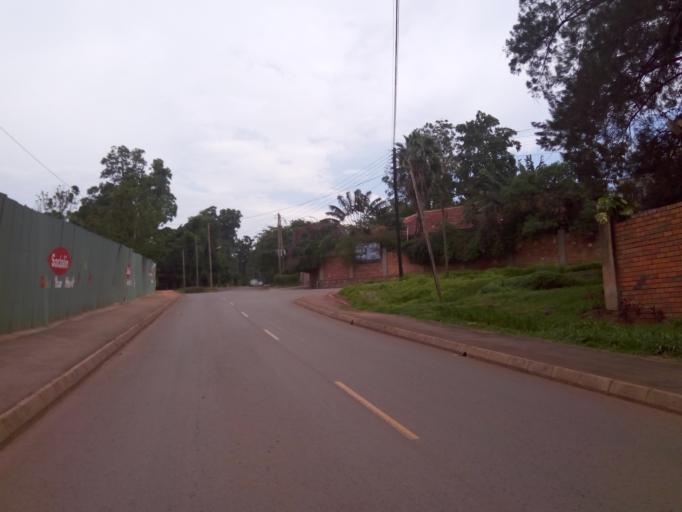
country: UG
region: Central Region
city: Kampala Central Division
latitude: 0.3293
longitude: 32.5806
